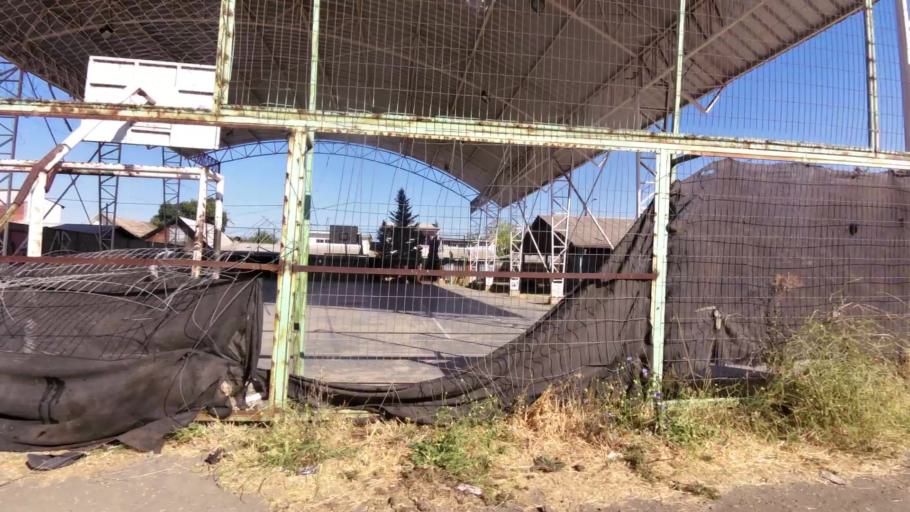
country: CL
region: Maule
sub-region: Provincia de Curico
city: Curico
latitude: -34.9969
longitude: -71.2594
